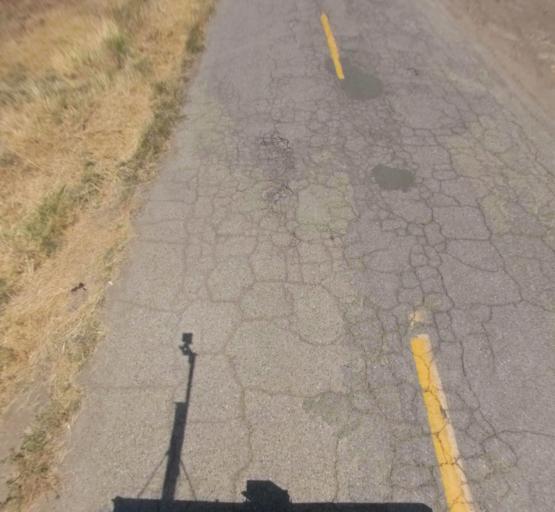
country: US
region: California
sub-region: Madera County
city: Chowchilla
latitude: 37.0944
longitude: -120.4370
